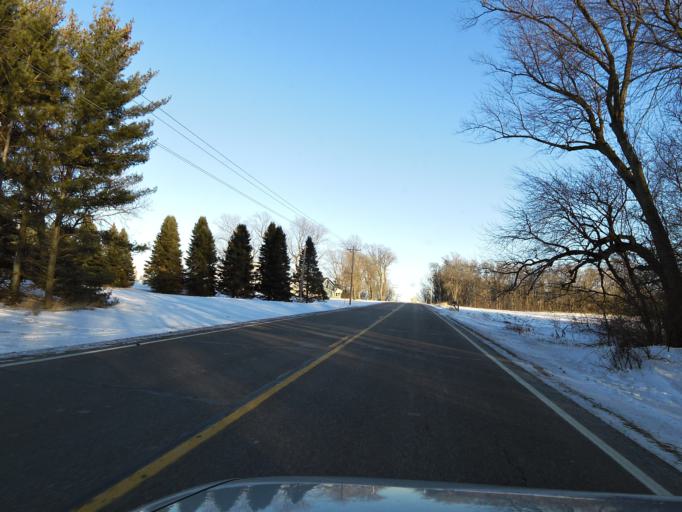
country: US
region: Minnesota
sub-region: Rice County
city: Northfield
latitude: 44.5438
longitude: -93.1762
